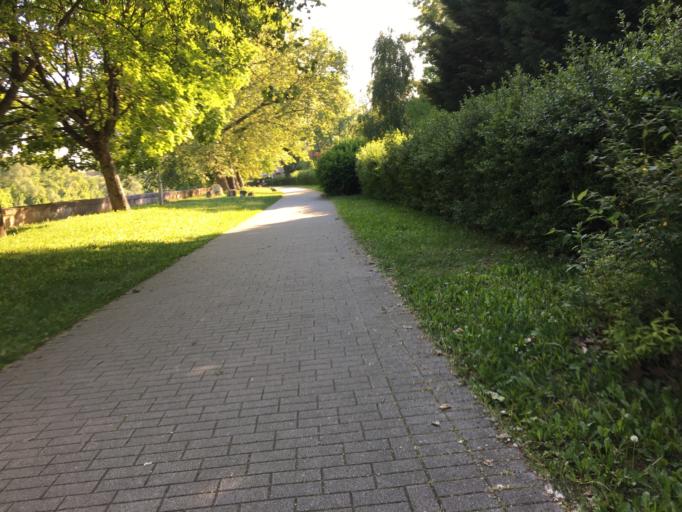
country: HU
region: Budapest
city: Budapest III. keruelet
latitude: 47.5601
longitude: 19.0560
